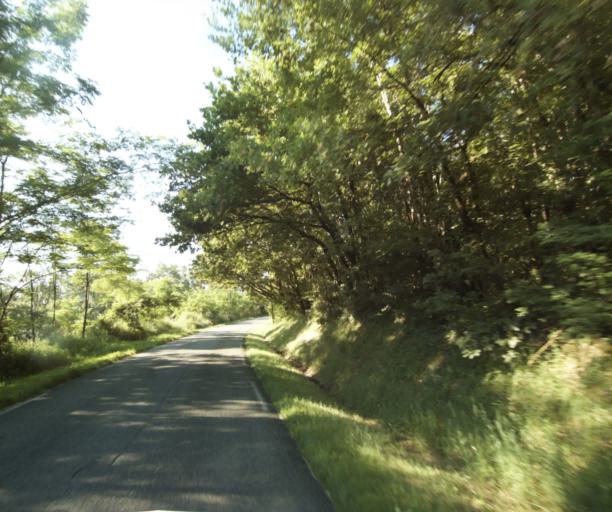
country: FR
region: Midi-Pyrenees
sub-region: Departement du Tarn-et-Garonne
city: Saint-Etienne-de-Tulmont
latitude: 44.0192
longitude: 1.4303
